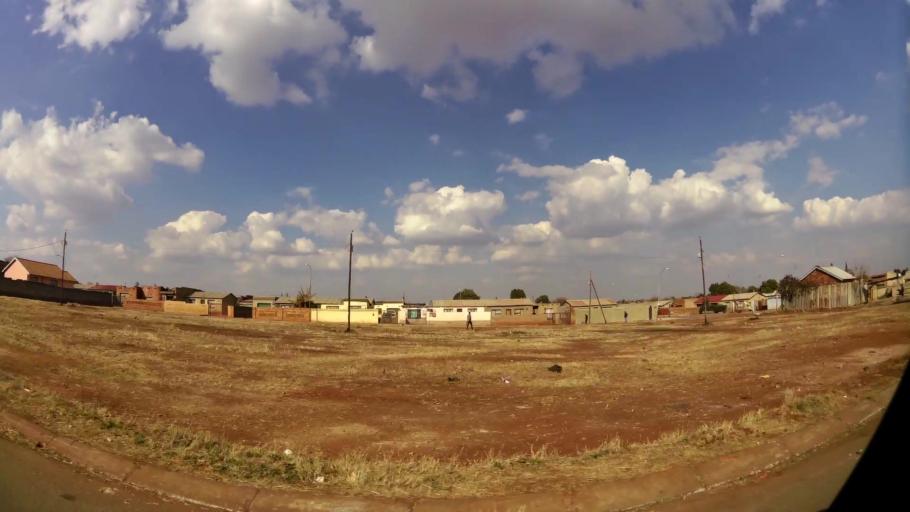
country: ZA
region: Gauteng
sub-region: City of Johannesburg Metropolitan Municipality
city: Soweto
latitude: -26.2191
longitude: 27.8616
